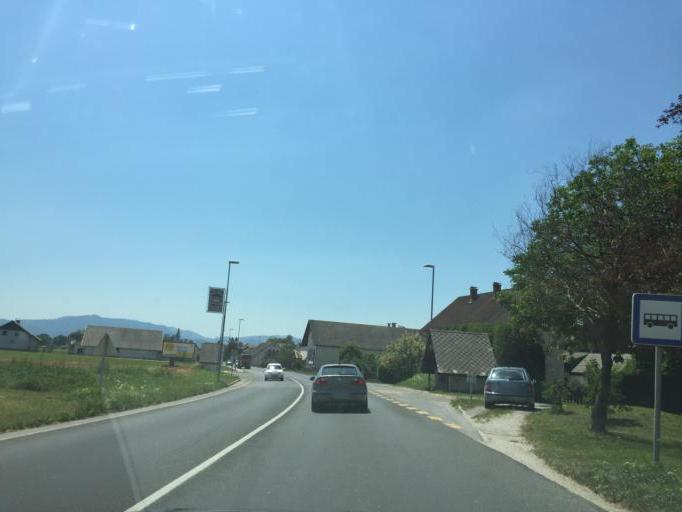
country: SI
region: Kranj
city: Zgornje Bitnje
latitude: 46.2208
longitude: 14.3396
